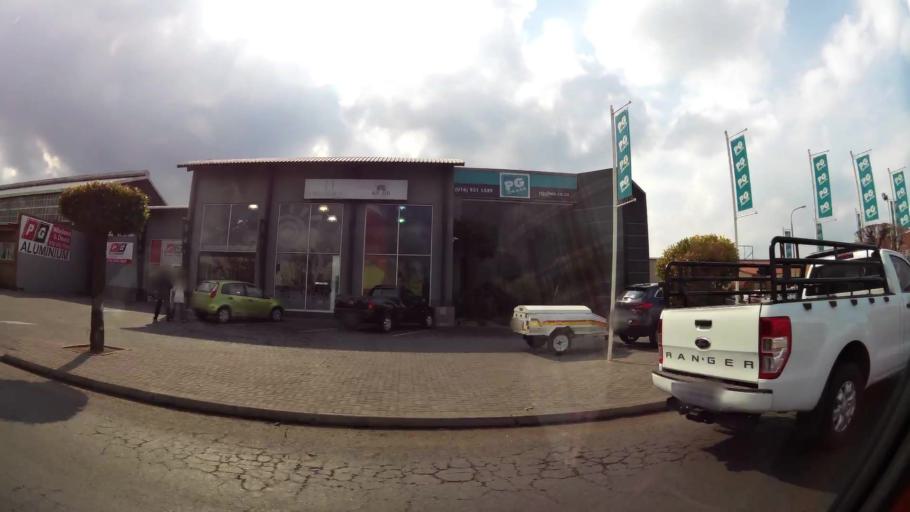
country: ZA
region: Gauteng
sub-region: Sedibeng District Municipality
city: Vanderbijlpark
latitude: -26.7057
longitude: 27.8526
